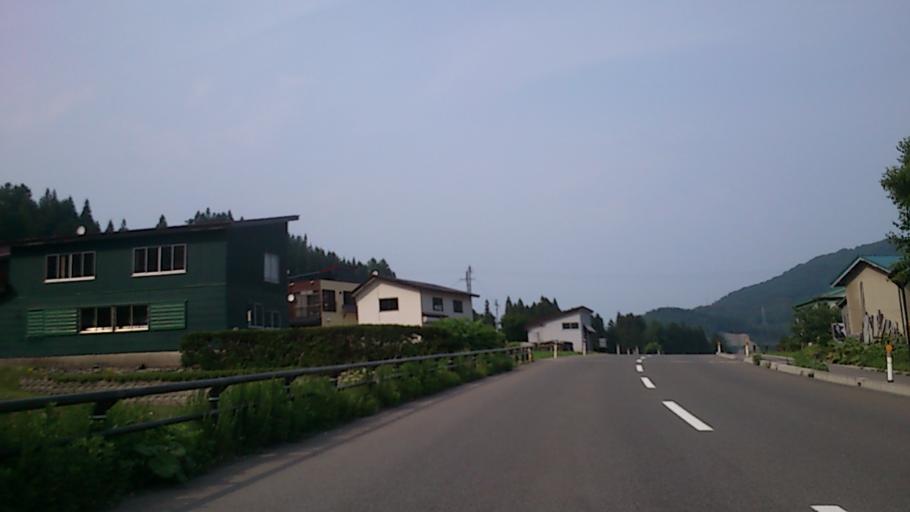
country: JP
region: Aomori
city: Hirosaki
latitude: 40.5489
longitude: 140.2739
